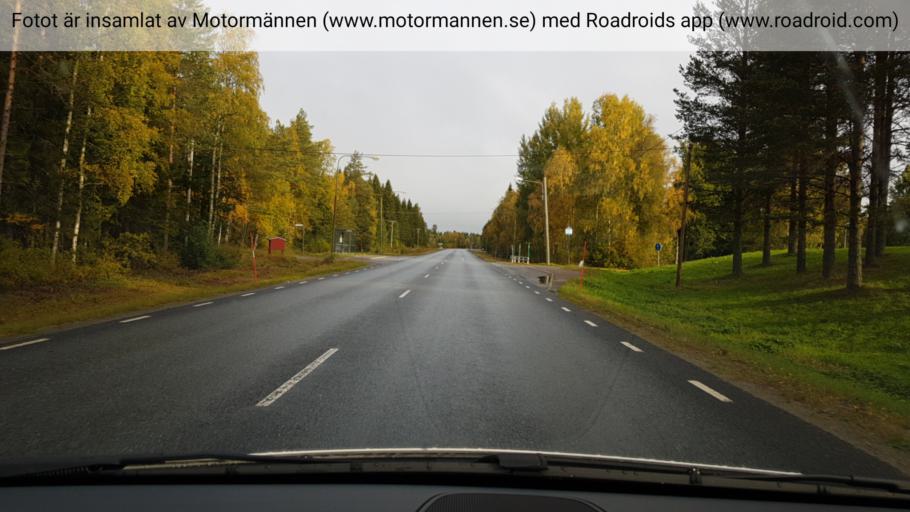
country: SE
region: Vaesterbotten
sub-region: Umea Kommun
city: Ersmark
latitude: 63.8798
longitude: 20.3068
